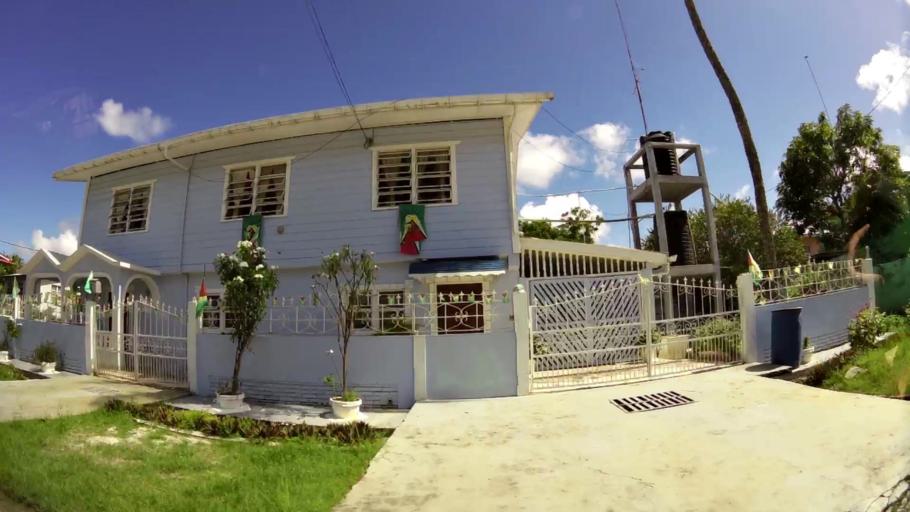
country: GY
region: Demerara-Mahaica
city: Georgetown
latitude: 6.7882
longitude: -58.1359
